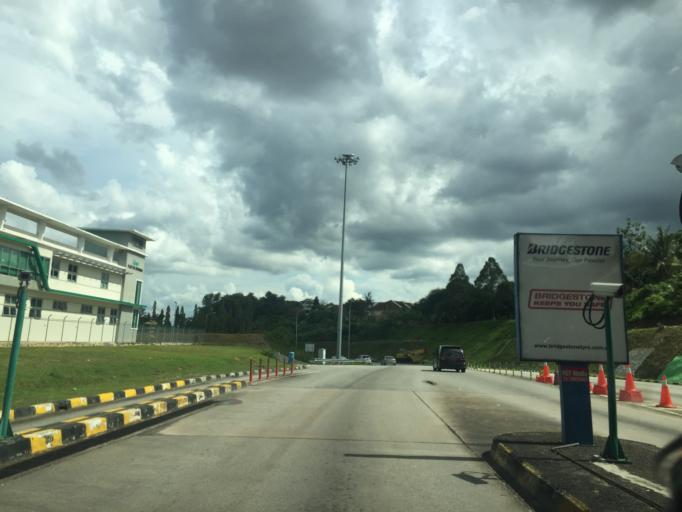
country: MY
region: Negeri Sembilan
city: Seremban
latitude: 2.7144
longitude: 101.9161
